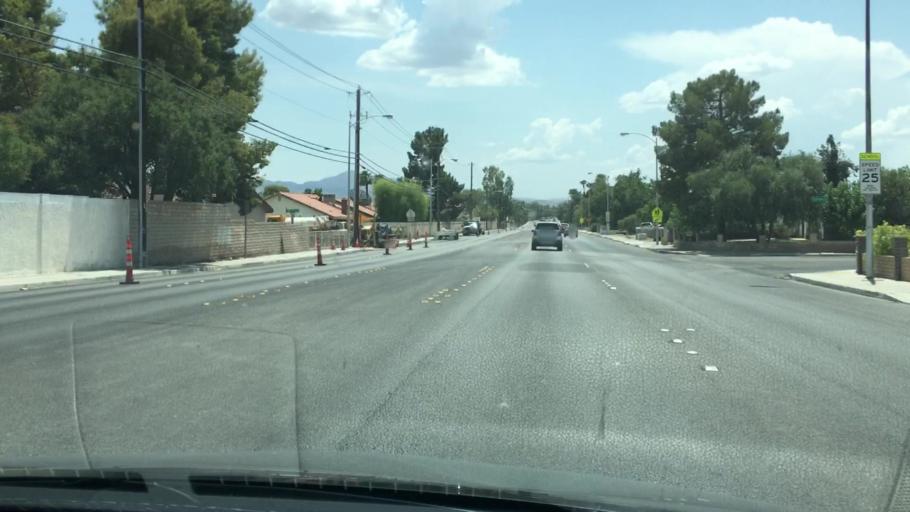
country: US
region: Nevada
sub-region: Clark County
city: Whitney
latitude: 36.0920
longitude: -115.0916
